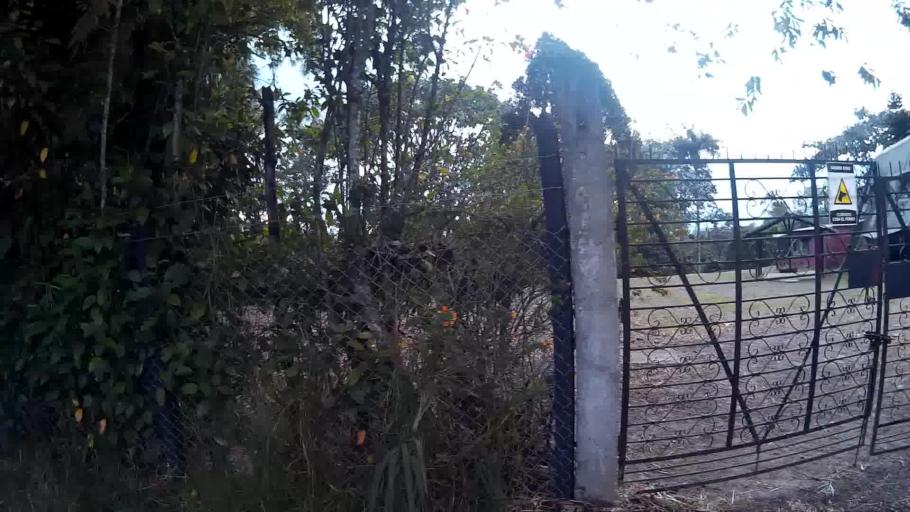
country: CO
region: Quindio
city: Filandia
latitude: 4.7181
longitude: -75.6240
